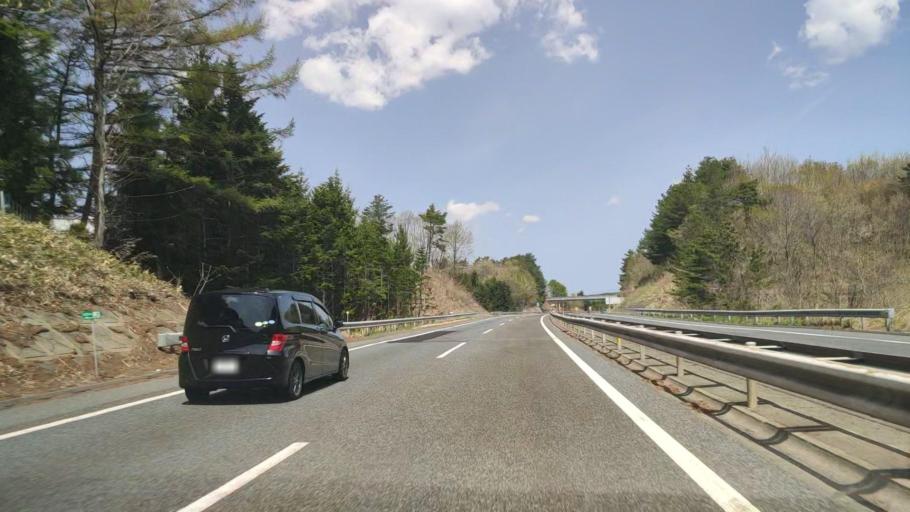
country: JP
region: Aomori
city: Hachinohe
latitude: 40.3453
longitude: 141.4487
